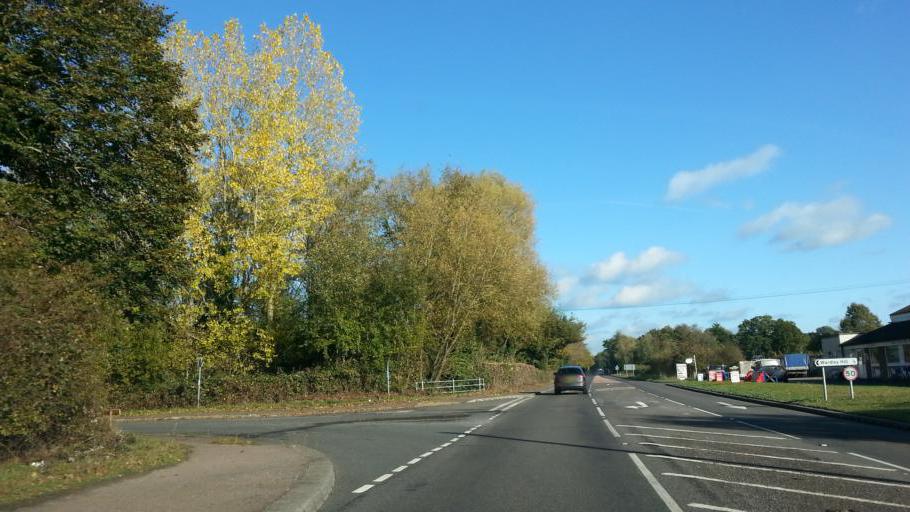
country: GB
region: England
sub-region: Norfolk
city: Ditchingham
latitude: 52.4803
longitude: 1.4793
